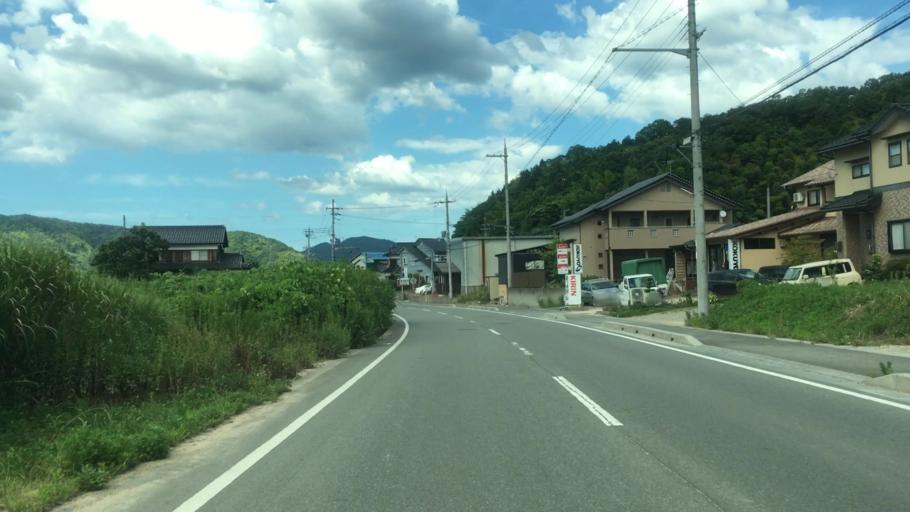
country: JP
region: Hyogo
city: Toyooka
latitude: 35.5524
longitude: 134.7924
